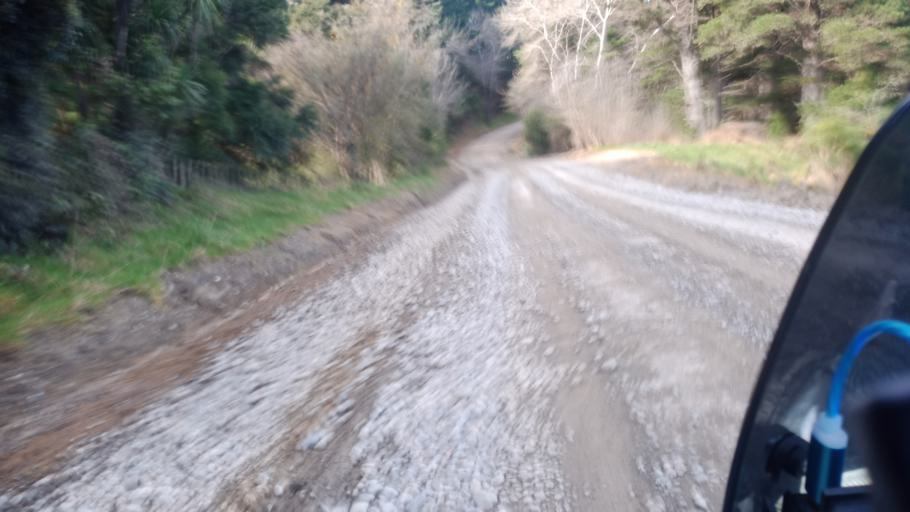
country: NZ
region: Gisborne
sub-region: Gisborne District
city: Gisborne
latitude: -38.1276
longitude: 178.1690
